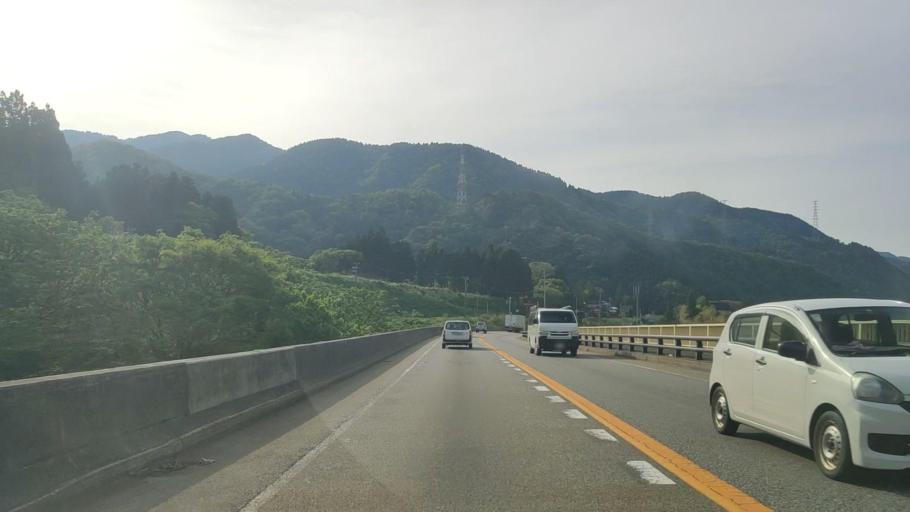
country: JP
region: Toyama
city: Yatsuomachi-higashikumisaka
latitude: 36.5053
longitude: 137.2316
